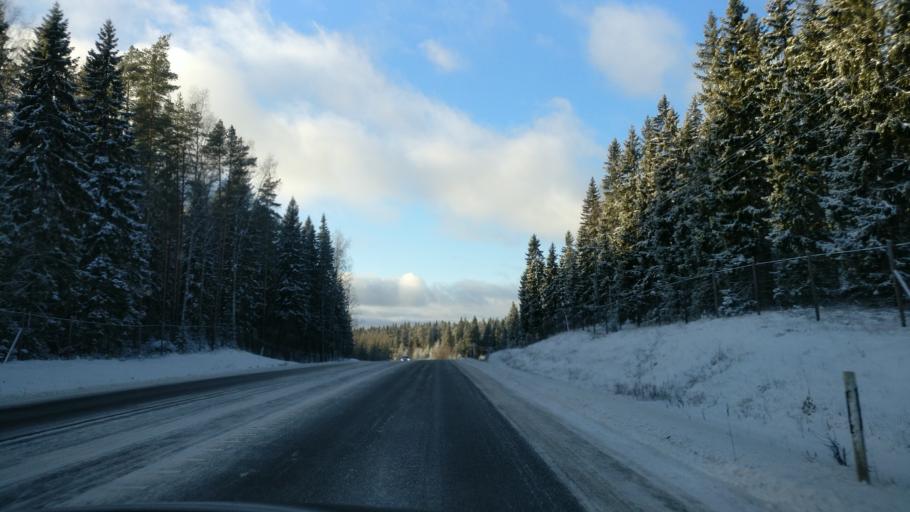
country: FI
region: Southern Savonia
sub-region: Mikkeli
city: Pertunmaa
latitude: 61.4370
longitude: 26.5015
